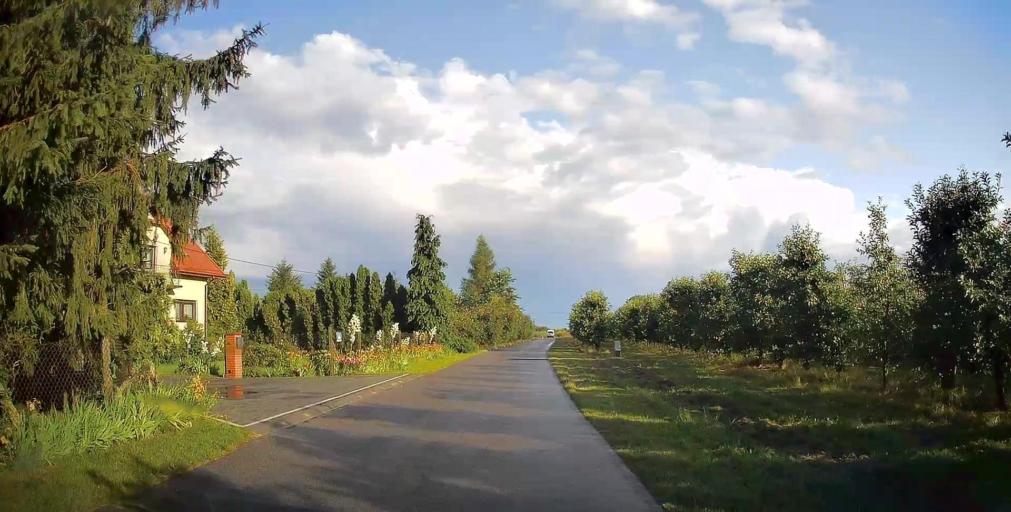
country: PL
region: Masovian Voivodeship
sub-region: Powiat grojecki
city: Goszczyn
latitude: 51.7521
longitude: 20.8844
